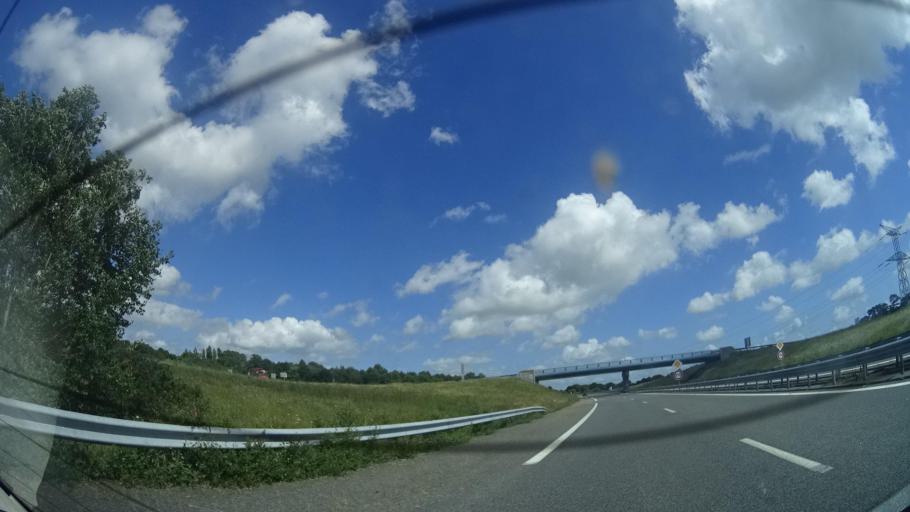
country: FR
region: Brittany
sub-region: Departement du Morbihan
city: Pluherlin
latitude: 47.6694
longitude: -2.3576
